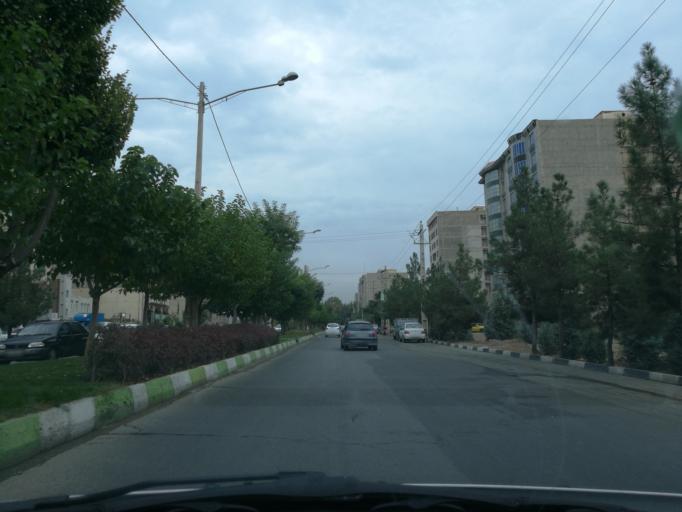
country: IR
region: Alborz
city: Karaj
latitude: 35.8570
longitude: 50.9504
